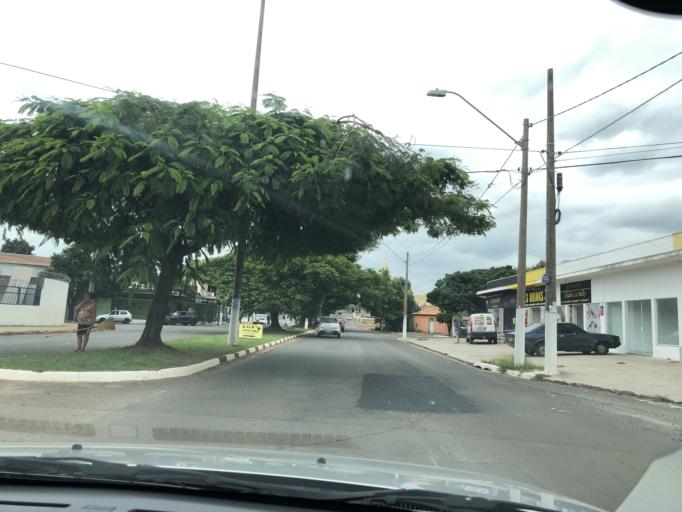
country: BR
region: Sao Paulo
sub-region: Paulinia
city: Paulinia
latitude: -22.7244
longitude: -47.1772
